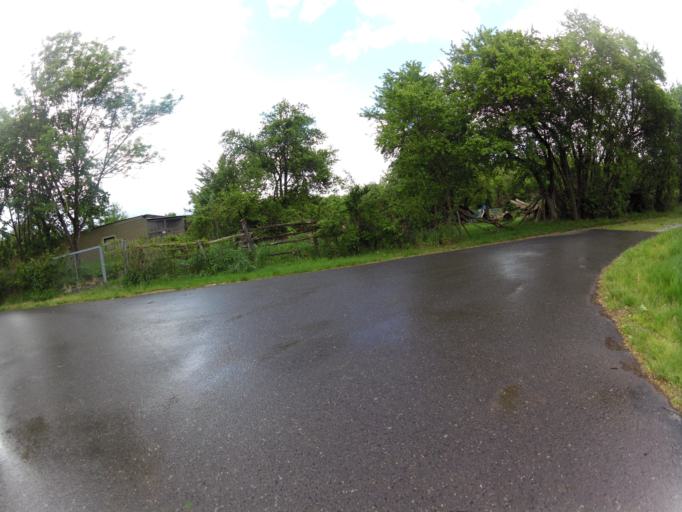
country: DE
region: Bavaria
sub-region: Regierungsbezirk Unterfranken
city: Volkach
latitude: 49.8681
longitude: 10.2433
